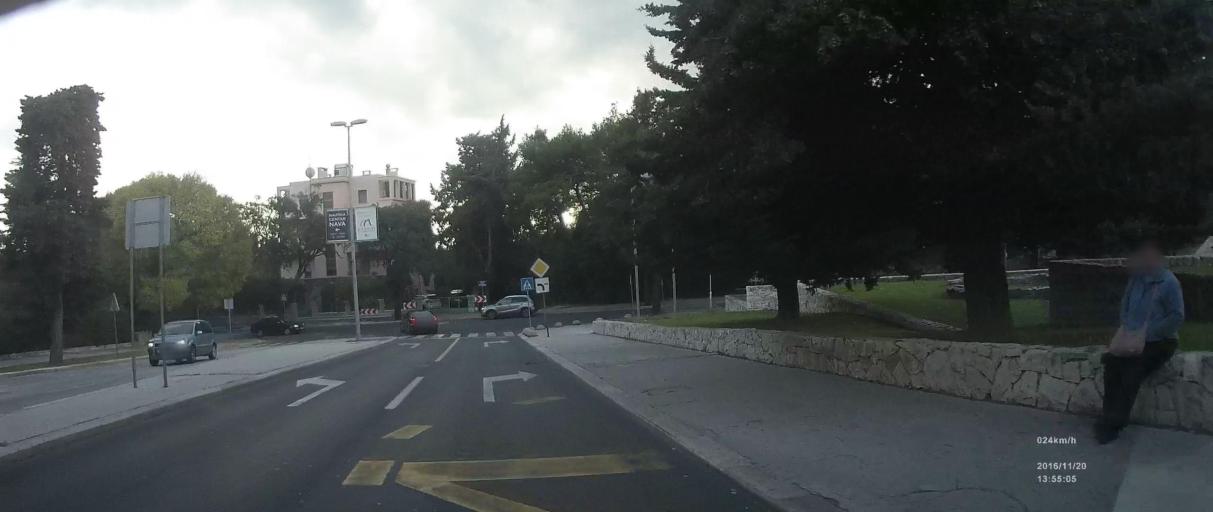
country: HR
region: Splitsko-Dalmatinska
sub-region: Grad Split
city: Split
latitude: 43.5043
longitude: 16.4234
